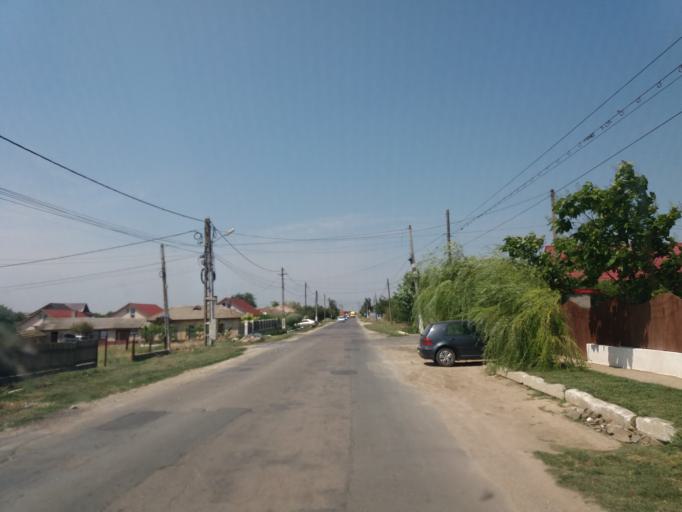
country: RO
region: Constanta
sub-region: Comuna Corbu
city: Corbu
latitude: 44.4019
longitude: 28.6616
